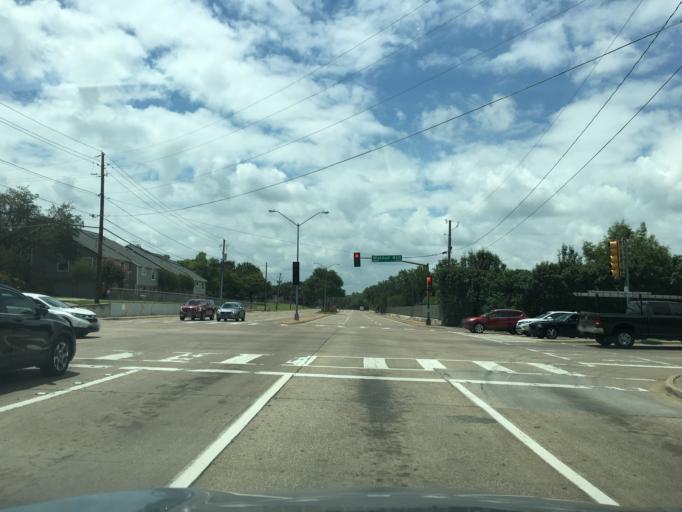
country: US
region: Texas
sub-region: Dallas County
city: University Park
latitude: 32.8807
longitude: -96.7417
